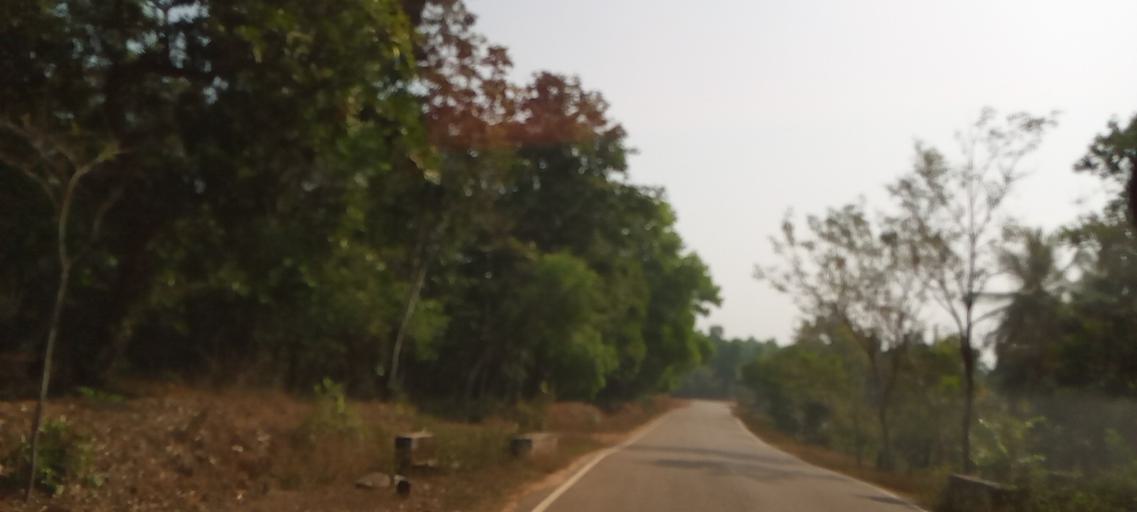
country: IN
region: Karnataka
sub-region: Udupi
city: Manipala
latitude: 13.5117
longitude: 74.8164
